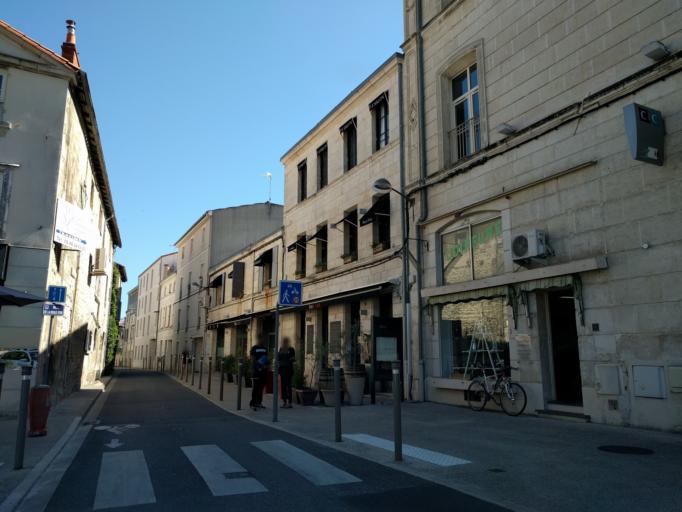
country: FR
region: Poitou-Charentes
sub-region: Departement des Deux-Sevres
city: Niort
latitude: 46.3243
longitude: -0.4582
